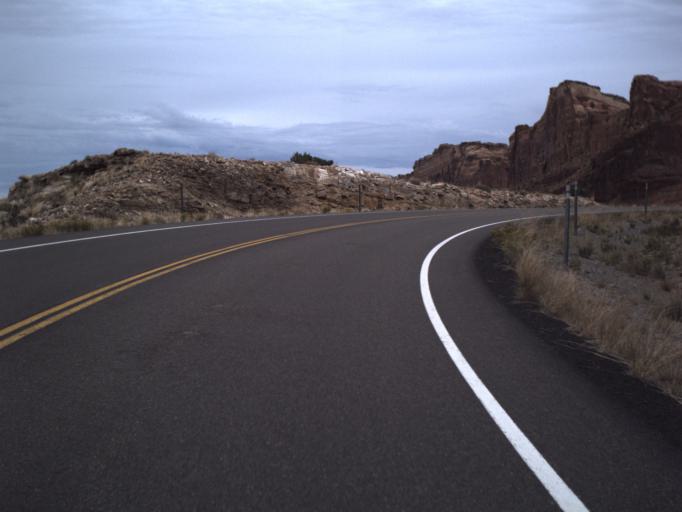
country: US
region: Utah
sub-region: Emery County
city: Castle Dale
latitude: 38.9349
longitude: -110.4746
